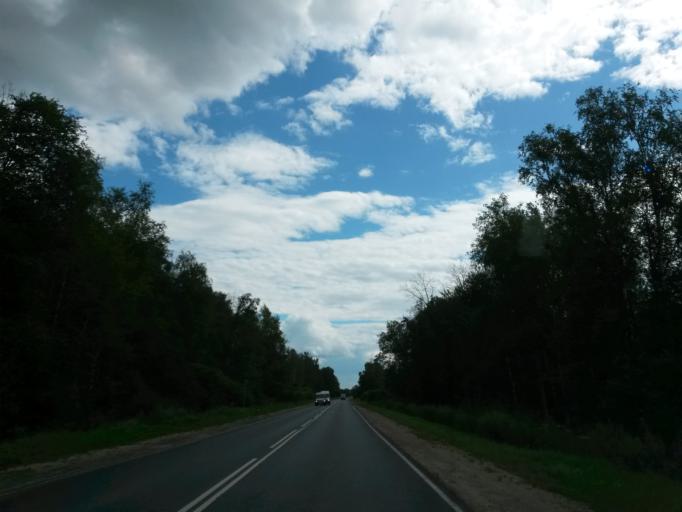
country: RU
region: Ivanovo
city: Novo-Talitsy
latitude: 57.0736
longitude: 40.6858
